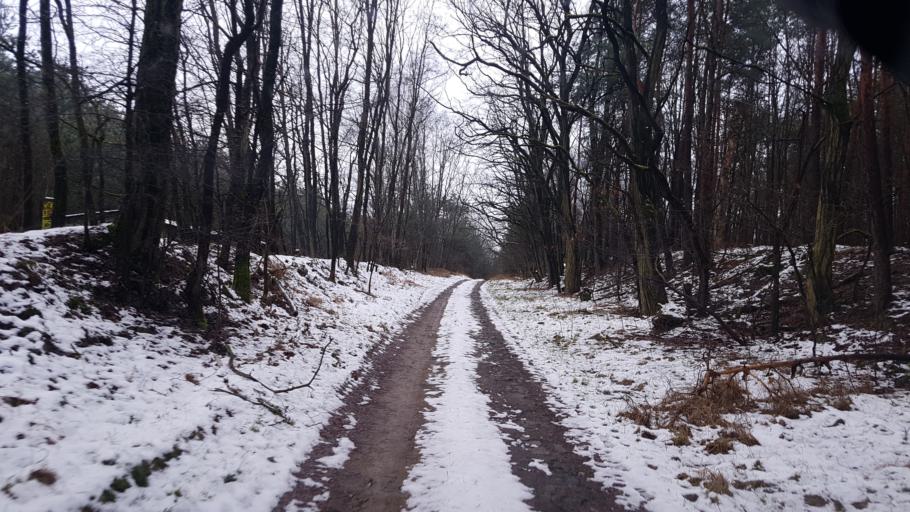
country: DE
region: Brandenburg
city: Jamlitz
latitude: 51.9957
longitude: 14.3699
